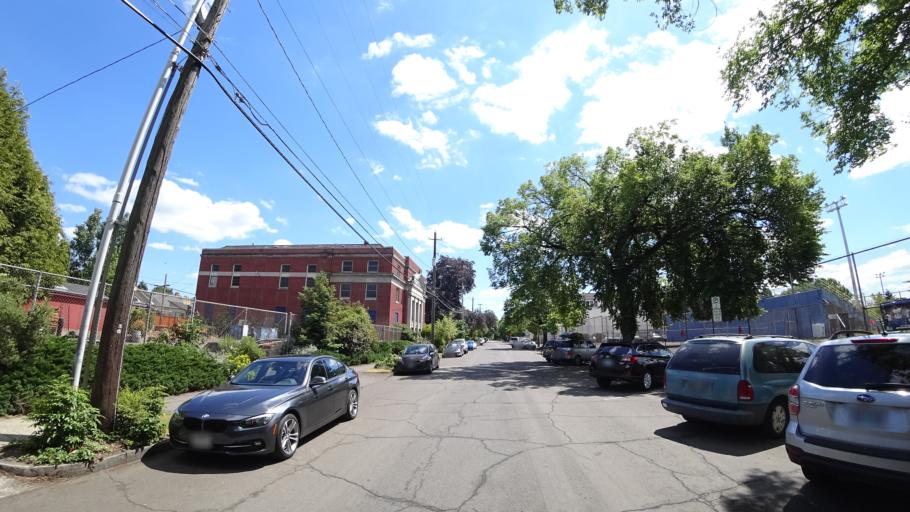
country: US
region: Oregon
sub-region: Multnomah County
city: Portland
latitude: 45.5624
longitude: -122.6711
